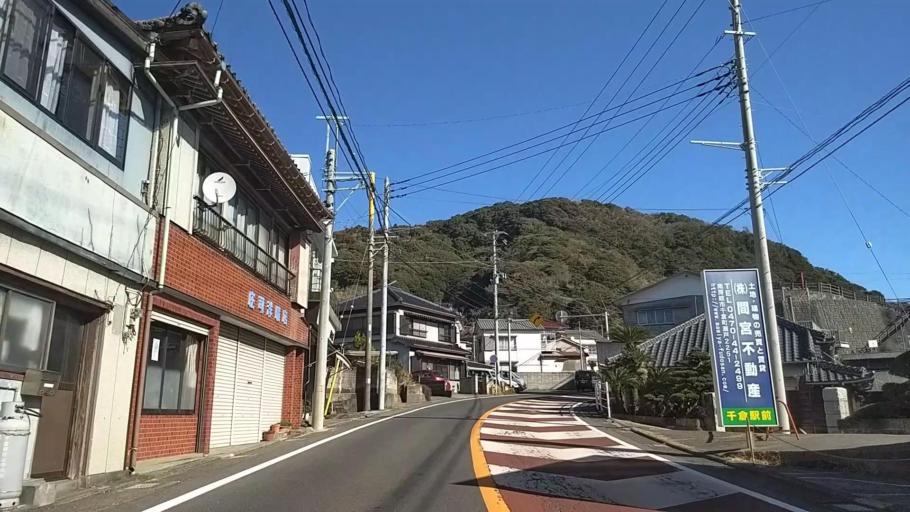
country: JP
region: Chiba
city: Kawaguchi
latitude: 35.0372
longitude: 140.0118
